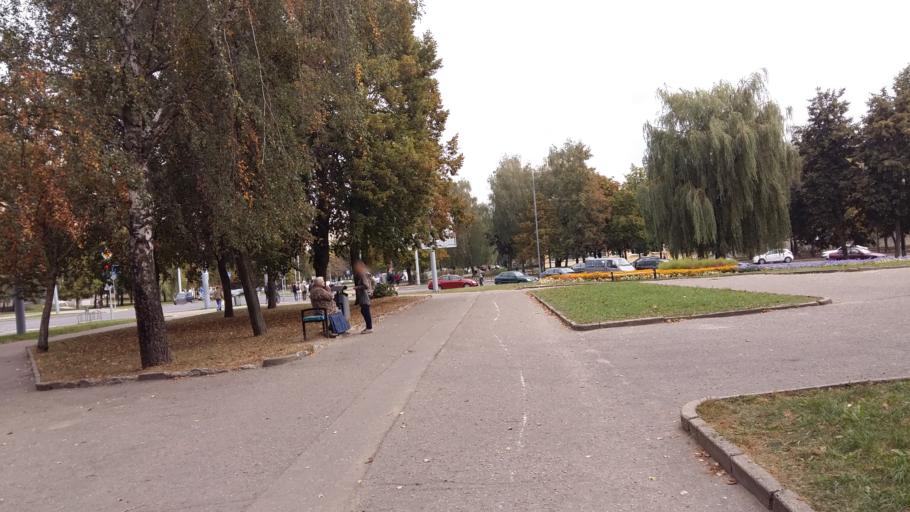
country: BY
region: Grodnenskaya
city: Hrodna
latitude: 53.6977
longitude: 23.8079
